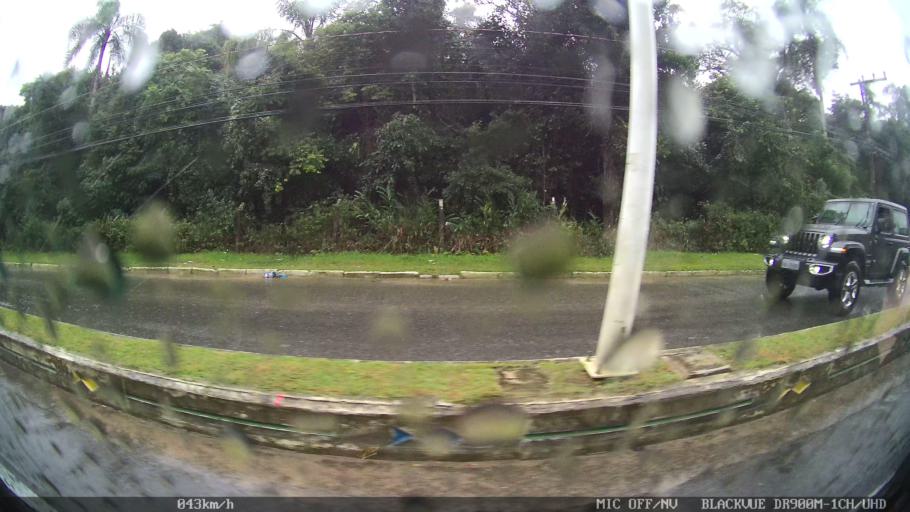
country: BR
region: Santa Catarina
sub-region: Itajai
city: Itajai
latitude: -26.9440
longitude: -48.6378
